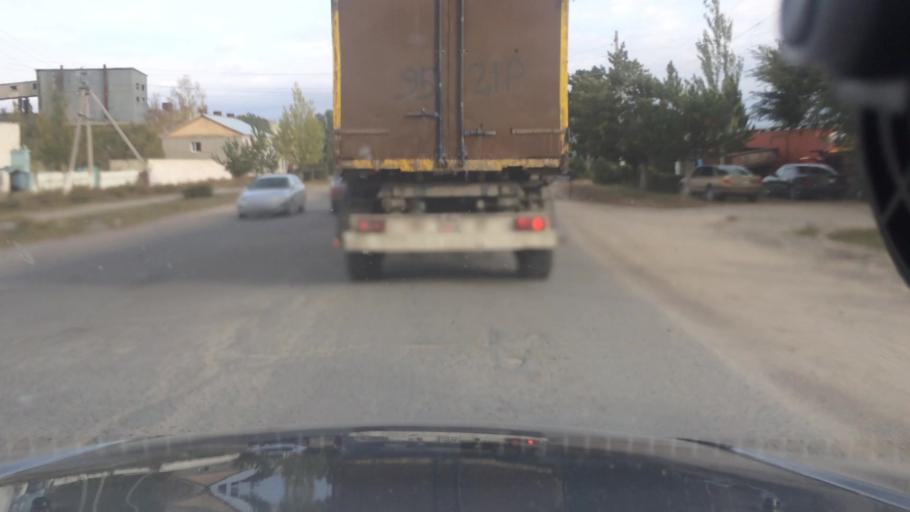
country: KG
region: Ysyk-Koel
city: Karakol
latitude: 42.5137
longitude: 78.3858
